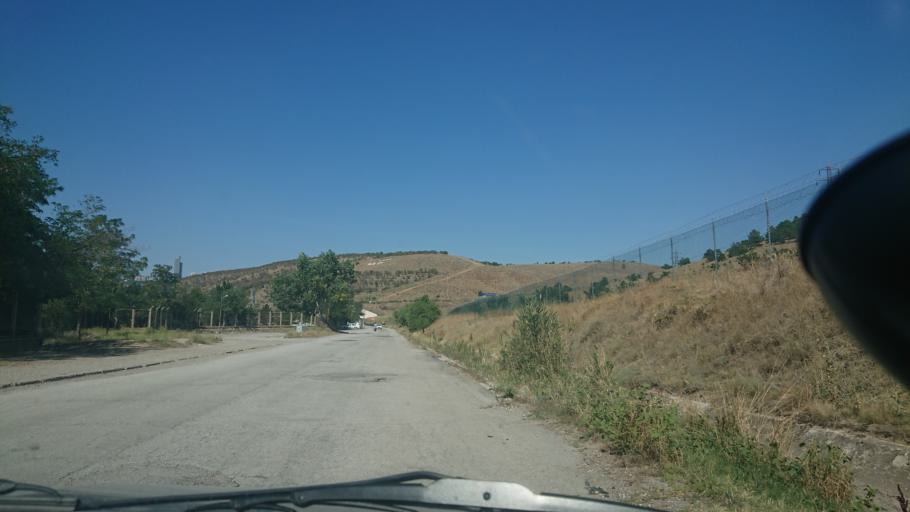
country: TR
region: Ankara
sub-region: Goelbasi
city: Golbasi
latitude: 39.8101
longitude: 32.8207
